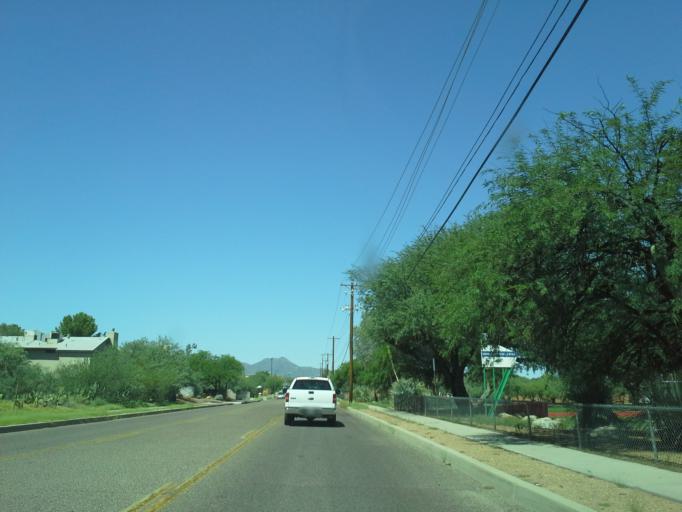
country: US
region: Arizona
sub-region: Pima County
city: Flowing Wells
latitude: 32.2830
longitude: -110.9659
